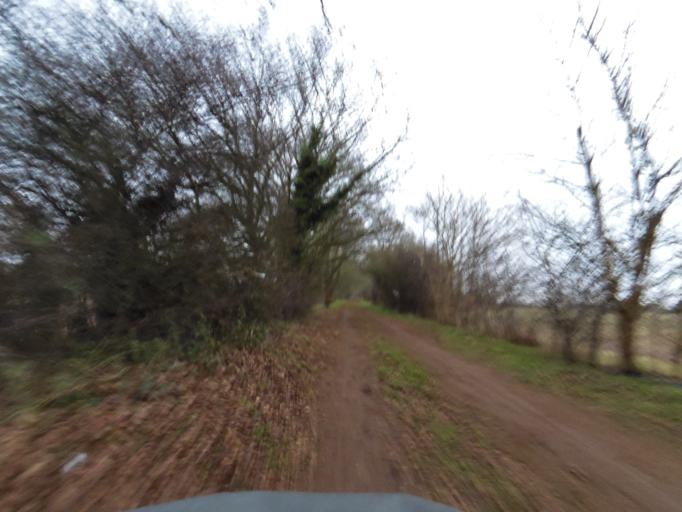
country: GB
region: England
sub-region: Norfolk
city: Horsford
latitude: 52.7004
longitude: 1.1987
